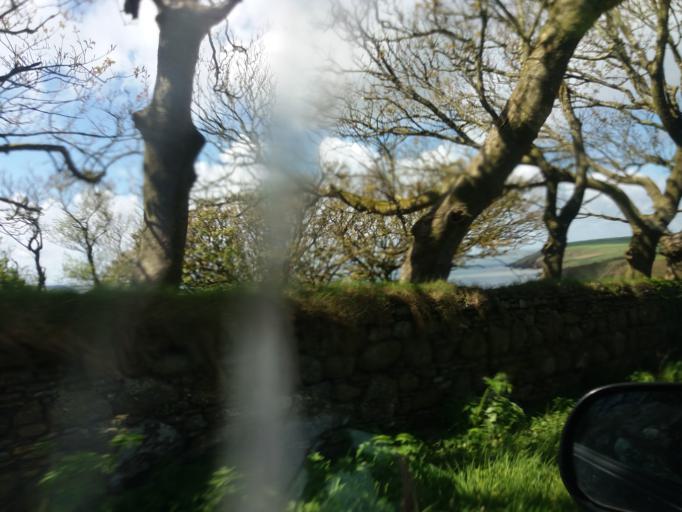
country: IE
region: Munster
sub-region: Waterford
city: Dunmore East
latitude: 52.1713
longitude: -6.8962
